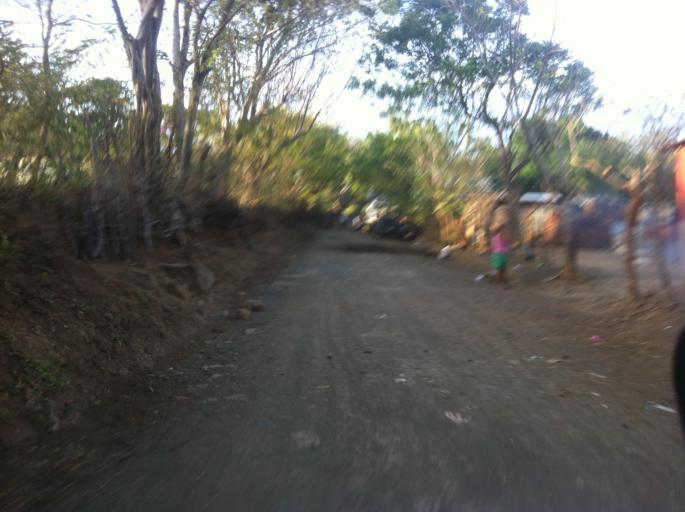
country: NI
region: Managua
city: Managua
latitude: 12.0846
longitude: -86.3114
